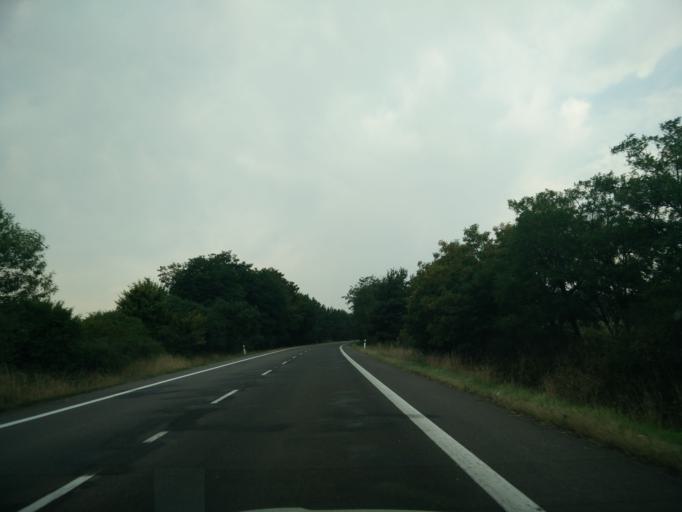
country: SK
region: Banskobystricky
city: Ziar nad Hronom
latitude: 48.6109
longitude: 18.8244
